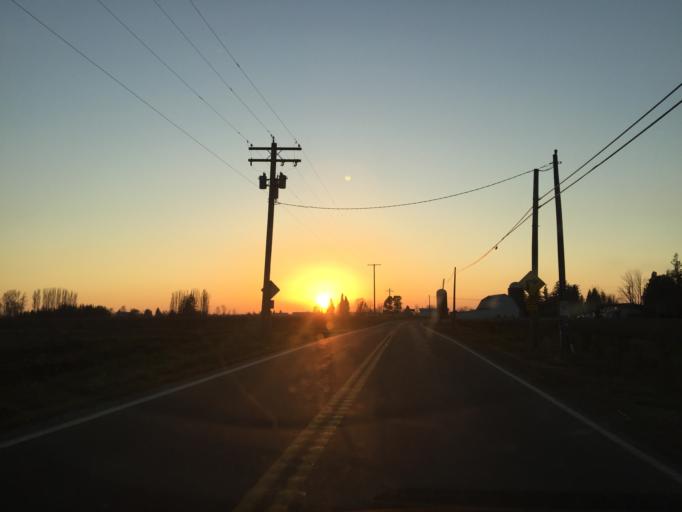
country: US
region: Washington
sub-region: Whatcom County
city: Sumas
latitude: 48.9819
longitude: -122.2394
